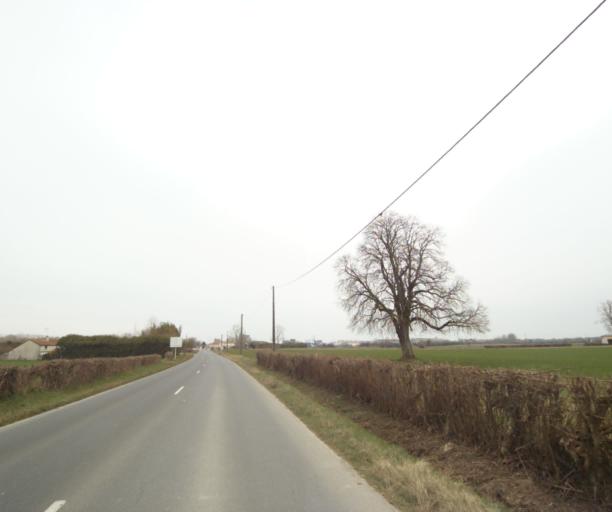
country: FR
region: Poitou-Charentes
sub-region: Departement des Deux-Sevres
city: Bessines
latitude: 46.3149
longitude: -0.5069
